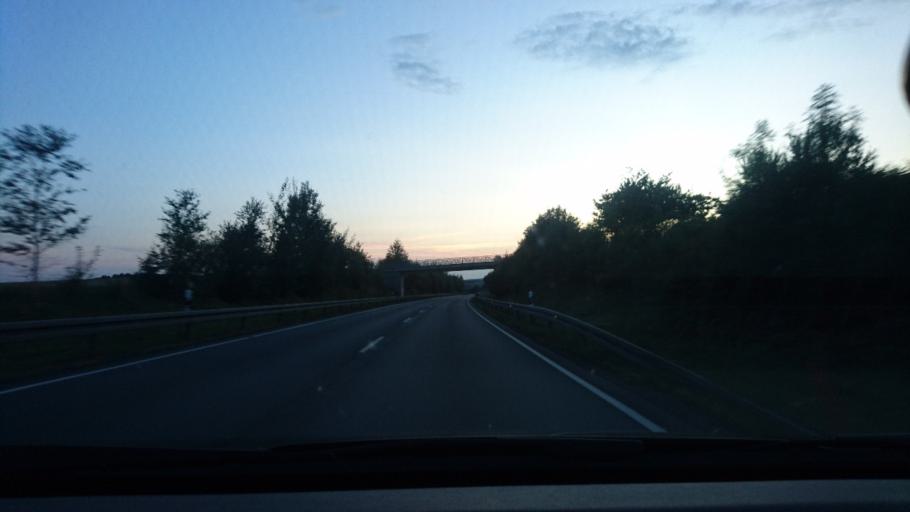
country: DE
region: Bavaria
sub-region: Upper Franconia
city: Selbitz
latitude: 50.3367
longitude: 11.7692
